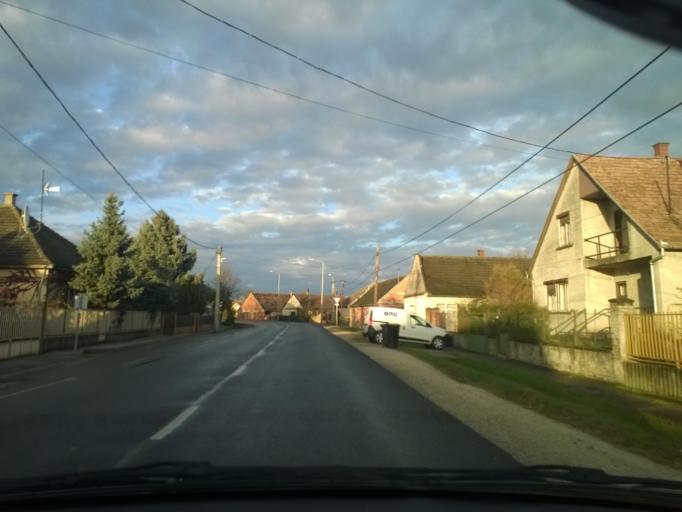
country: HU
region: Bacs-Kiskun
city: Dunapataj
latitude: 46.6356
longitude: 19.0035
